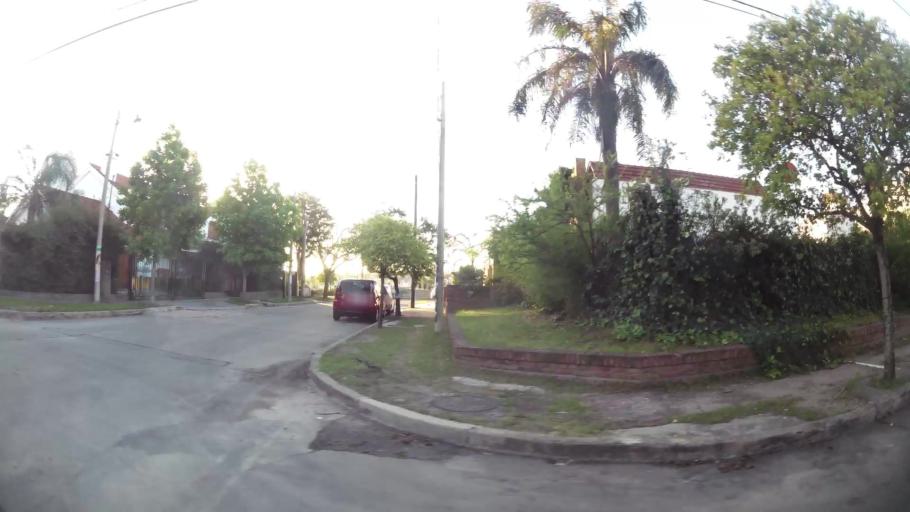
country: AR
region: Cordoba
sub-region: Departamento de Capital
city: Cordoba
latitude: -31.3825
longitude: -64.2132
